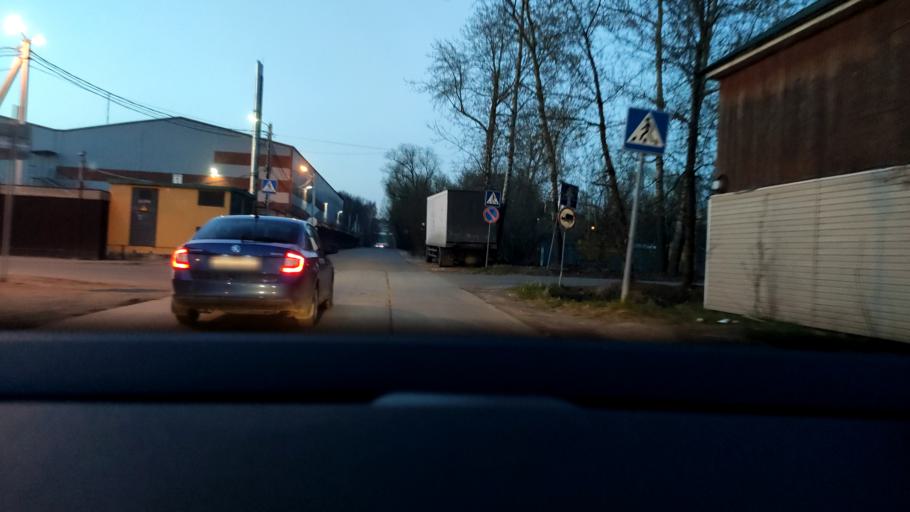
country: RU
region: Moskovskaya
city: Reutov
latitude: 55.7727
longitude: 37.8843
